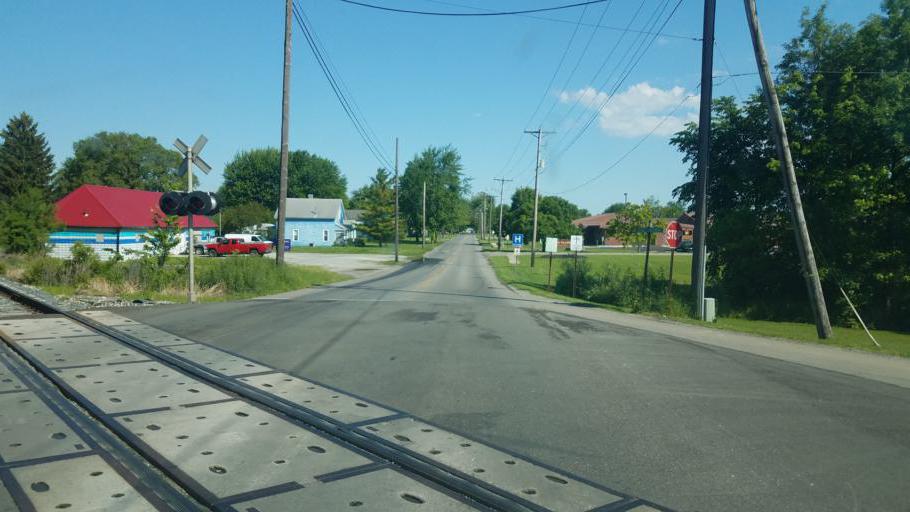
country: US
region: Ohio
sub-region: Hardin County
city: Kenton
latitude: 40.6351
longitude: -83.6027
